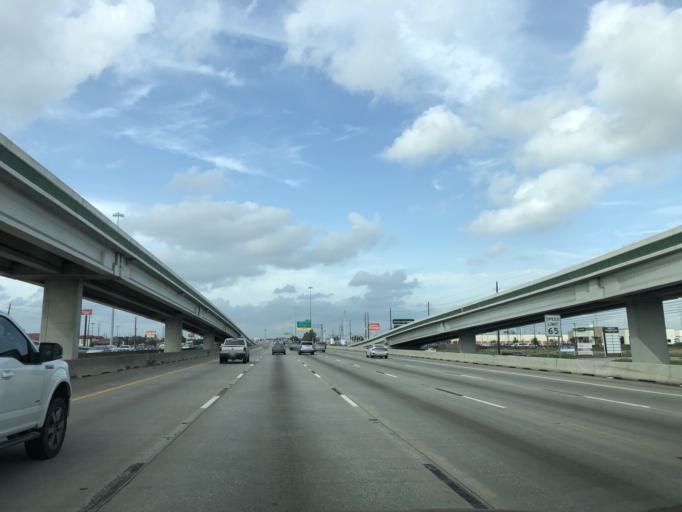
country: US
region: Texas
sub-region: Harris County
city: Spring
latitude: 30.0127
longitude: -95.4279
